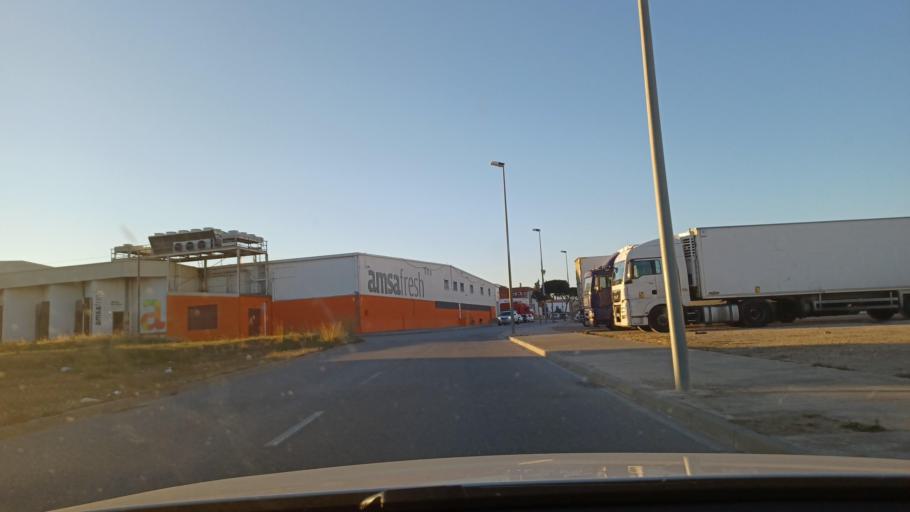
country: ES
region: Catalonia
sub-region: Provincia de Tarragona
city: Amposta
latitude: 40.6997
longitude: 0.5770
